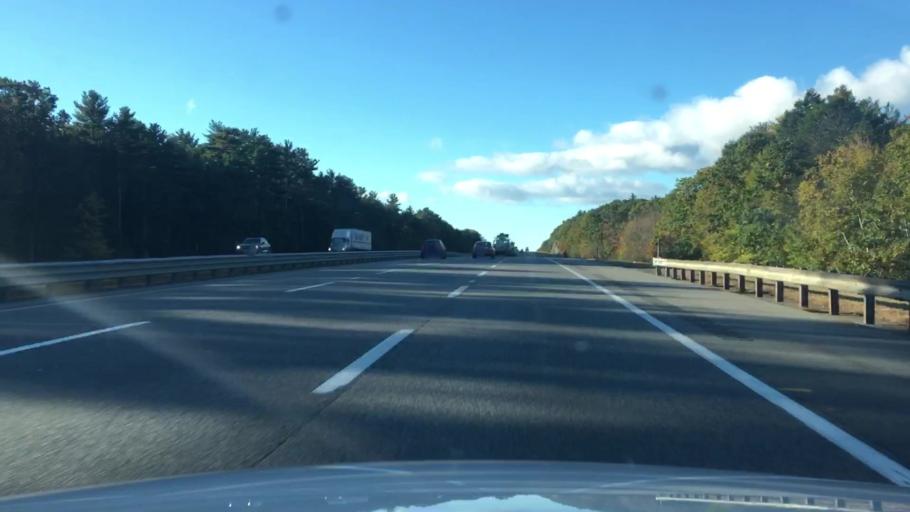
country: US
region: Maine
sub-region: York County
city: Cape Neddick
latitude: 43.2207
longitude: -70.6381
